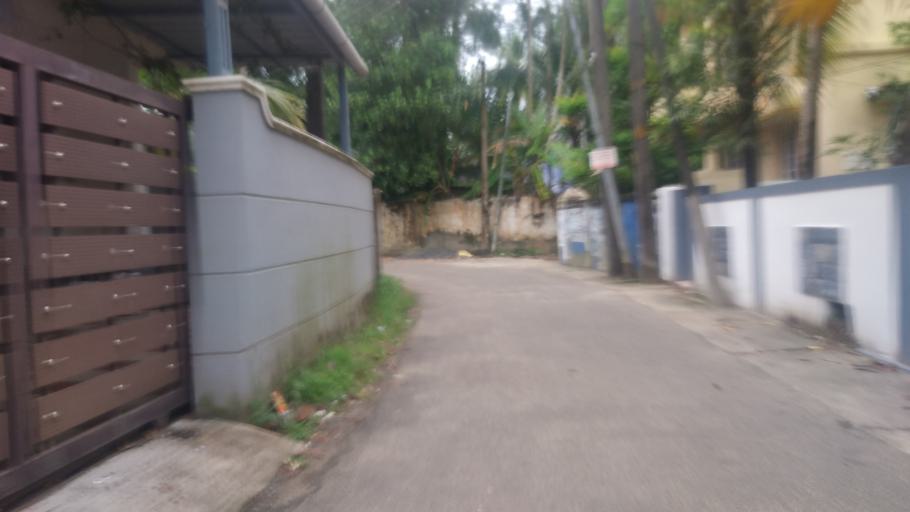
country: IN
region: Kerala
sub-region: Alappuzha
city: Arukutti
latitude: 9.8729
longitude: 76.2879
